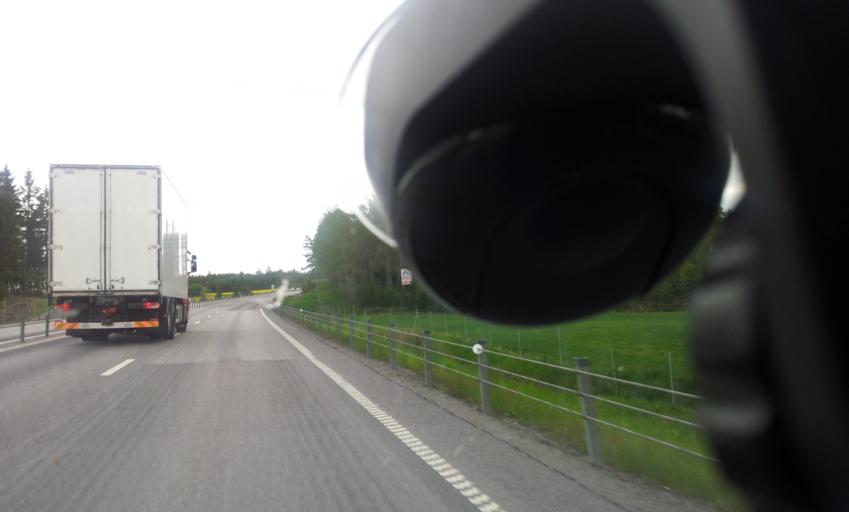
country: SE
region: OEstergoetland
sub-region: Valdemarsviks Kommun
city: Gusum
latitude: 58.3047
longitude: 16.4887
